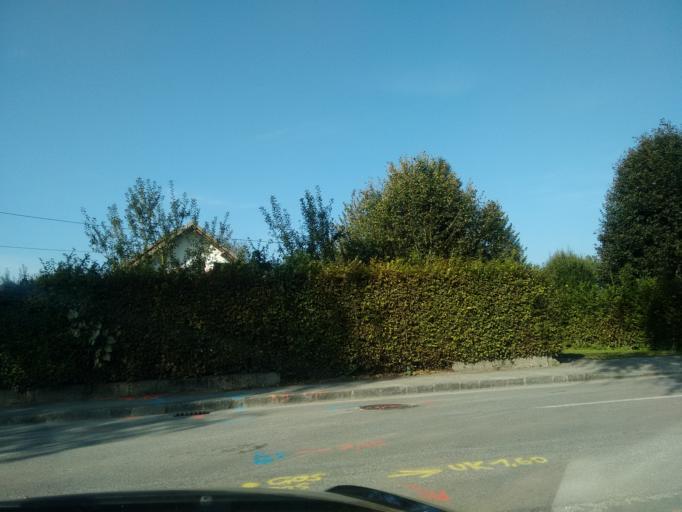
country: AT
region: Upper Austria
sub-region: Politischer Bezirk Ried im Innkreis
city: Ried im Innkreis
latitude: 48.3087
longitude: 13.6313
